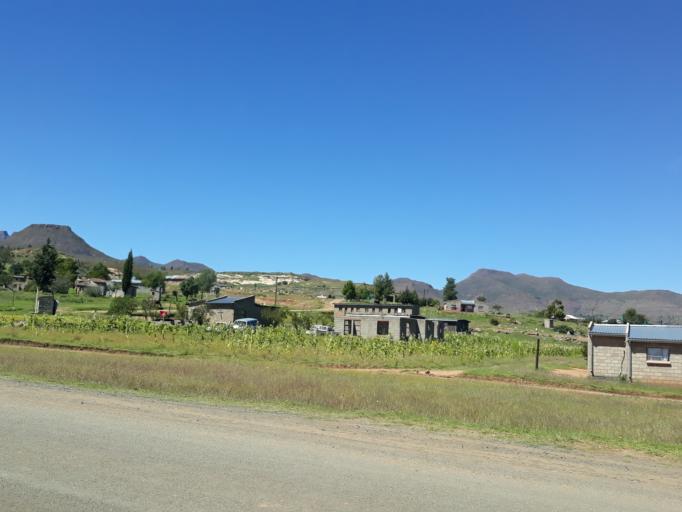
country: LS
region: Mohale's Hoek District
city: Mohale's Hoek
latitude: -30.1080
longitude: 27.4732
